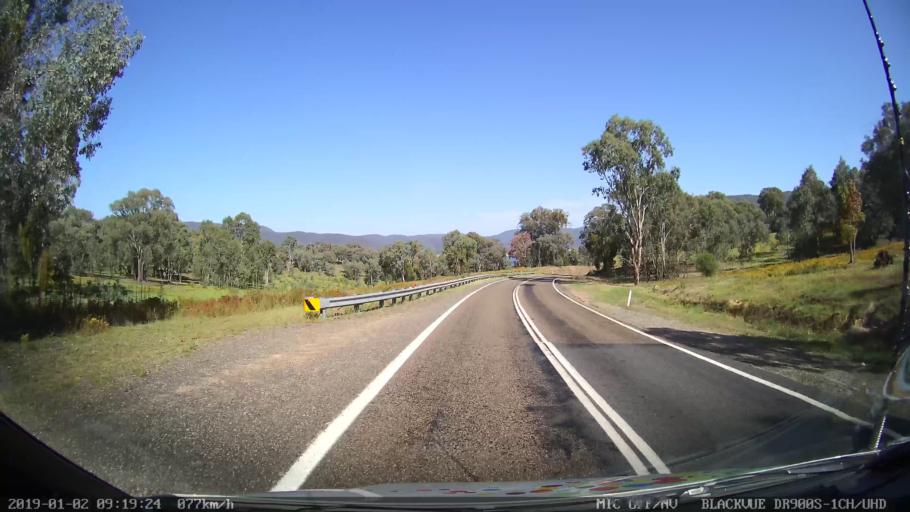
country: AU
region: New South Wales
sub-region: Tumut Shire
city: Tumut
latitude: -35.4222
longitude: 148.2786
